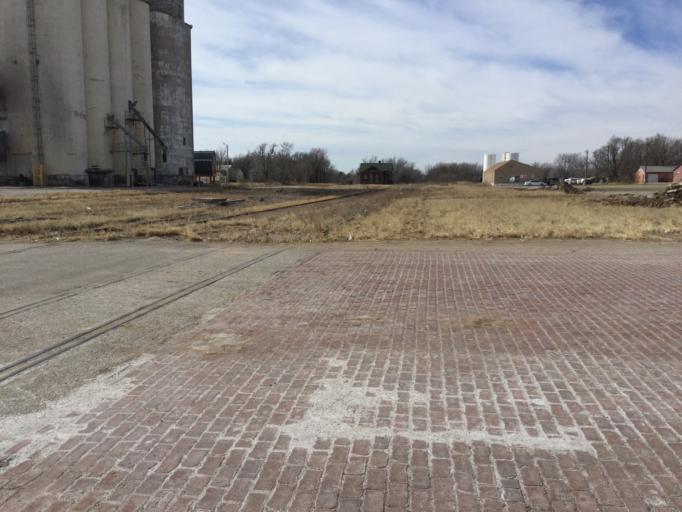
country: US
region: Kansas
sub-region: Rice County
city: Lyons
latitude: 38.3513
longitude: -98.2032
